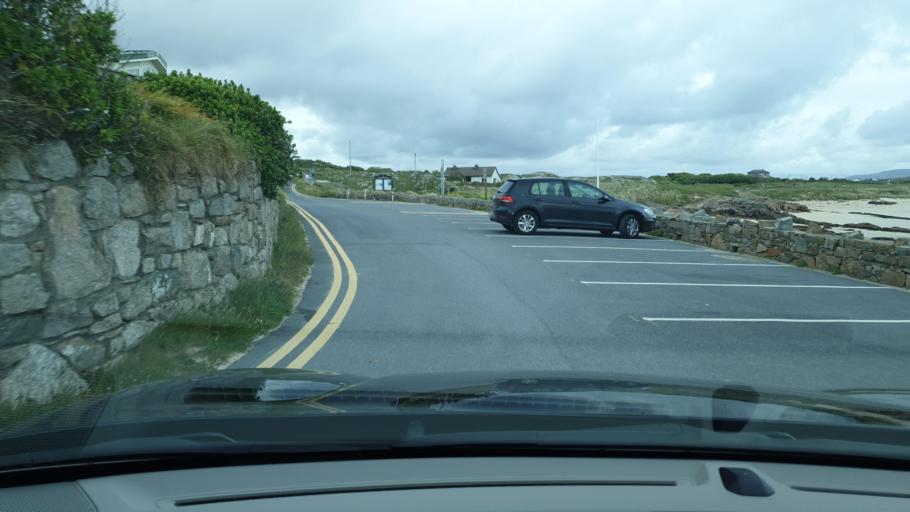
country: IE
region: Connaught
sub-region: County Galway
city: Clifden
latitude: 53.3810
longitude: -9.9540
